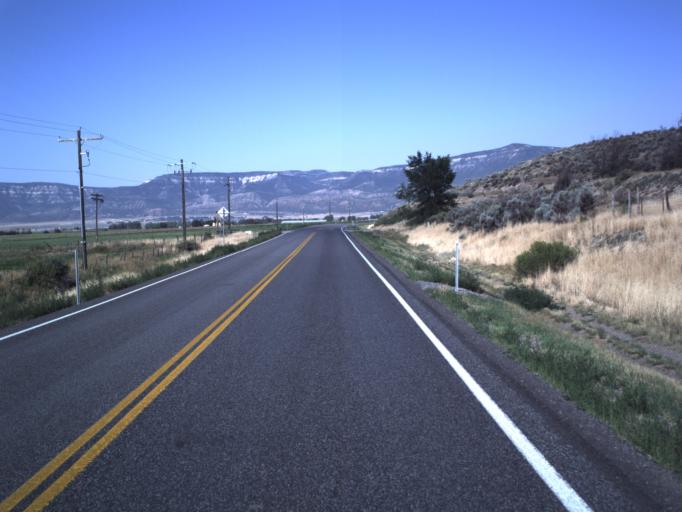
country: US
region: Utah
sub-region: Sanpete County
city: Moroni
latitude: 39.5272
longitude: -111.5494
